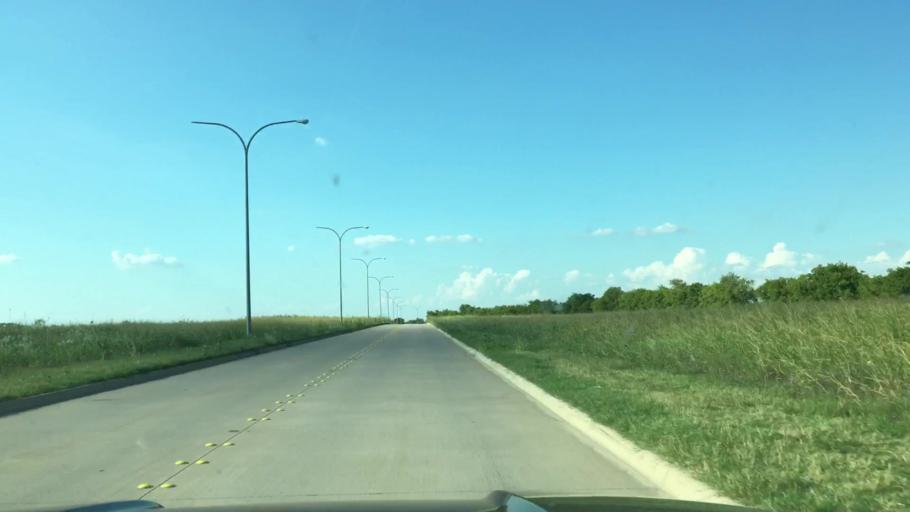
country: US
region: Texas
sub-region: Tarrant County
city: Haslet
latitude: 33.0004
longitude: -97.3587
